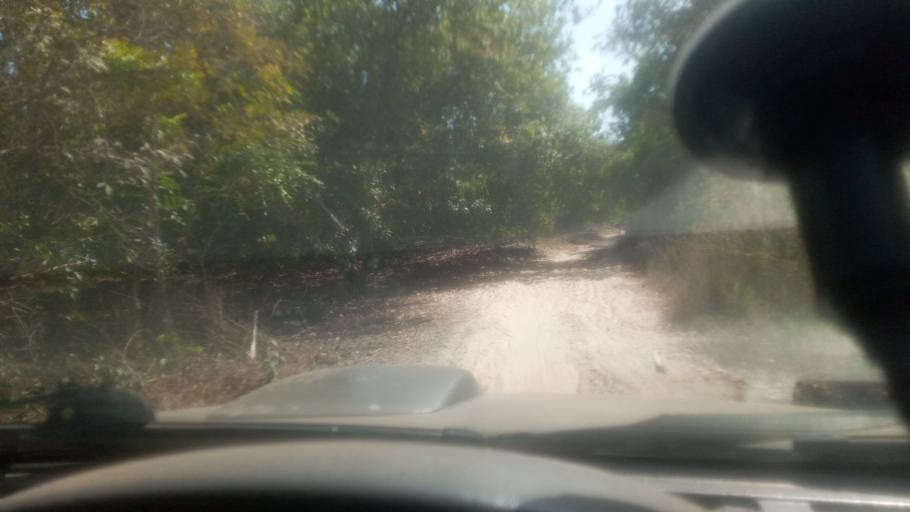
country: GW
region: Oio
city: Farim
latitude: 12.4551
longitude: -15.4099
